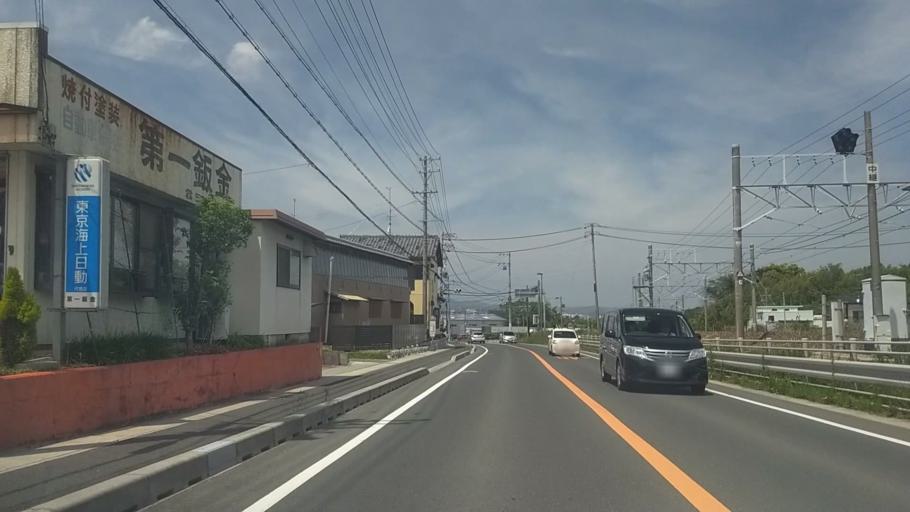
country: JP
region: Shizuoka
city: Kosai-shi
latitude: 34.6995
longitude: 137.5562
